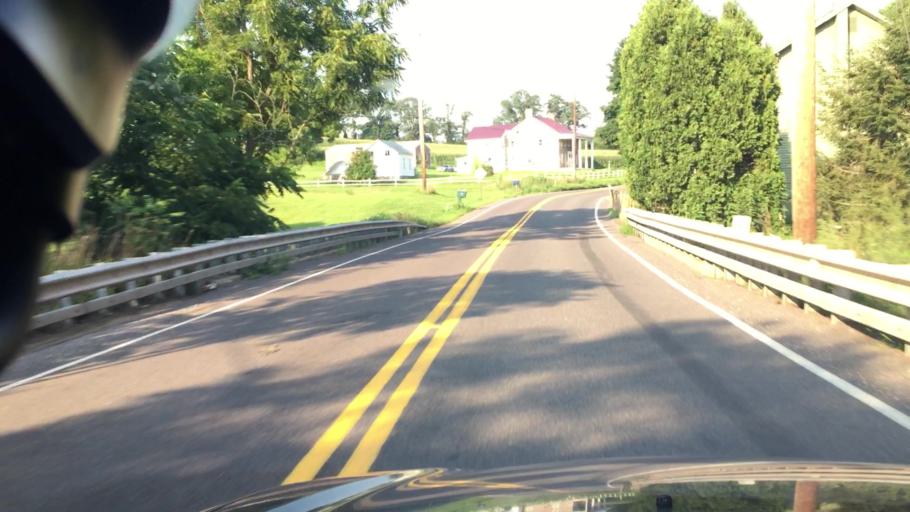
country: US
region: Pennsylvania
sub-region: Columbia County
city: Almedia
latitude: 40.9904
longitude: -76.3496
